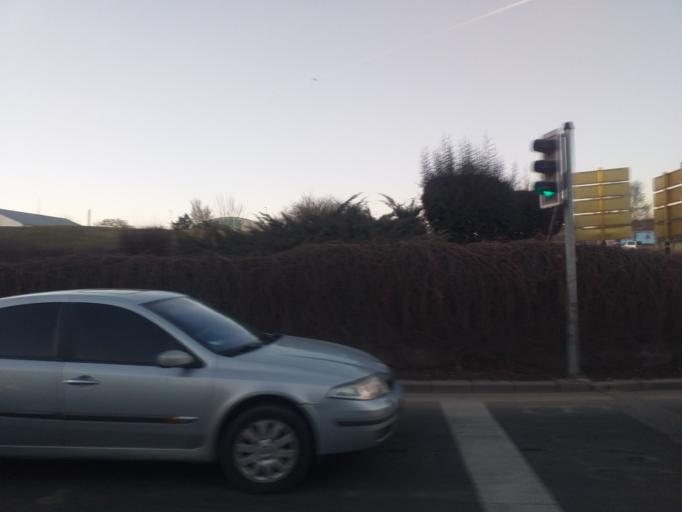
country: TR
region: Ankara
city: Ankara
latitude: 39.9577
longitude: 32.8235
